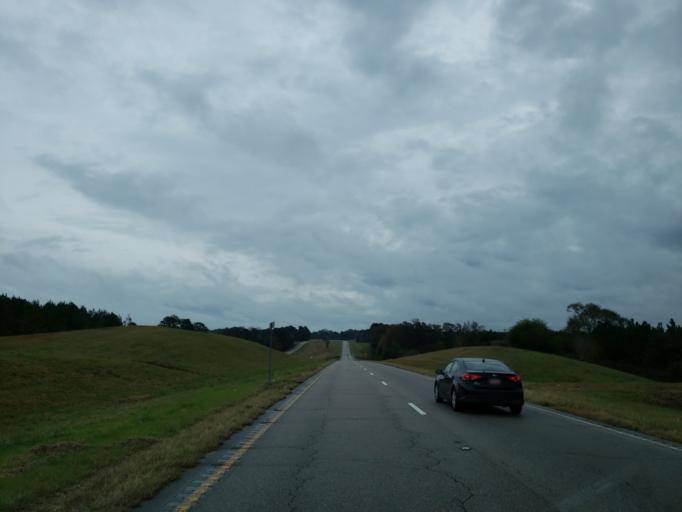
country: US
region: Mississippi
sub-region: Jones County
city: Sharon
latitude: 31.7009
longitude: -88.9048
